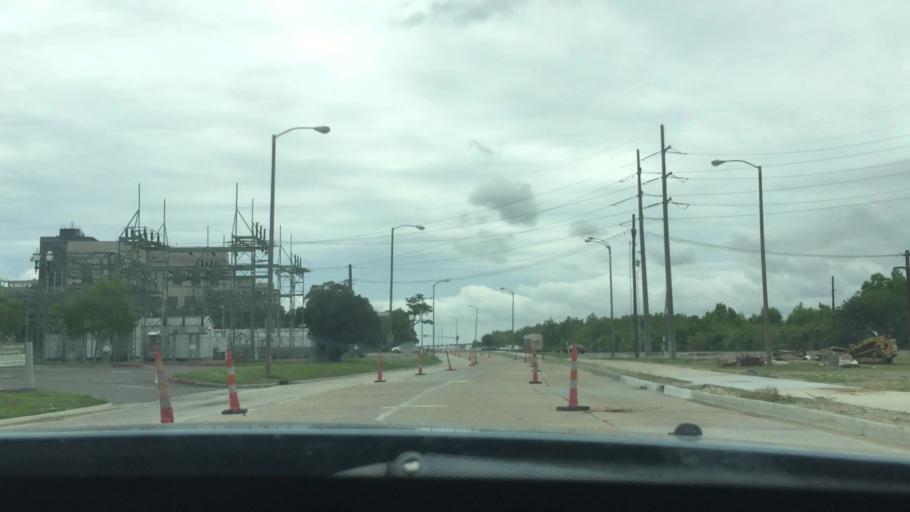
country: US
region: Louisiana
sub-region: West Baton Rouge Parish
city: Port Allen
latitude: 30.4592
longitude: -91.1896
